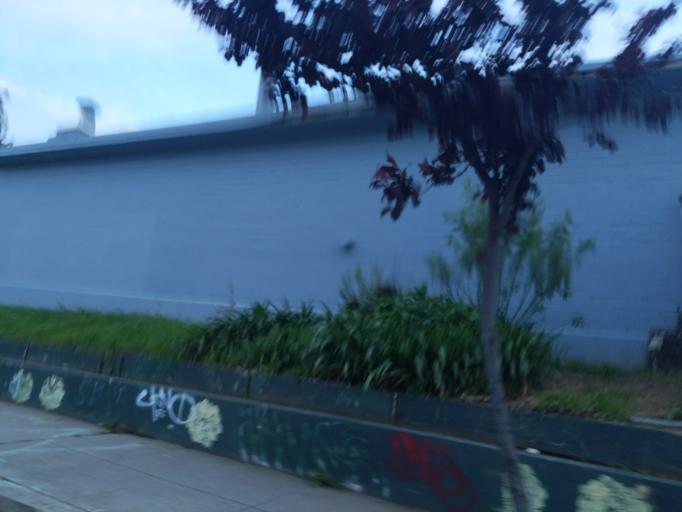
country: US
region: California
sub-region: Alameda County
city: Emeryville
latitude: 37.8129
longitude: -122.2883
